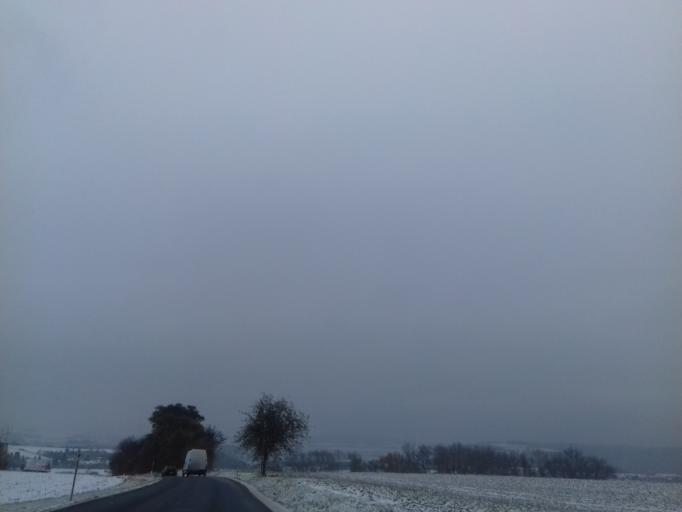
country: CZ
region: Plzensky
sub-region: Okres Domazlice
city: Domazlice
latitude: 49.4630
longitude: 12.9345
